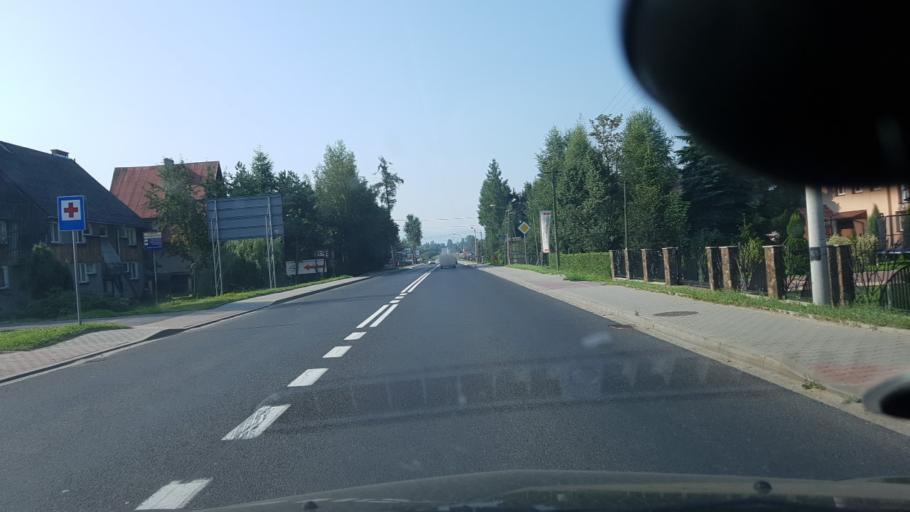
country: PL
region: Lesser Poland Voivodeship
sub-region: Powiat nowotarski
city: Jablonka
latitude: 49.4743
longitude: 19.6929
